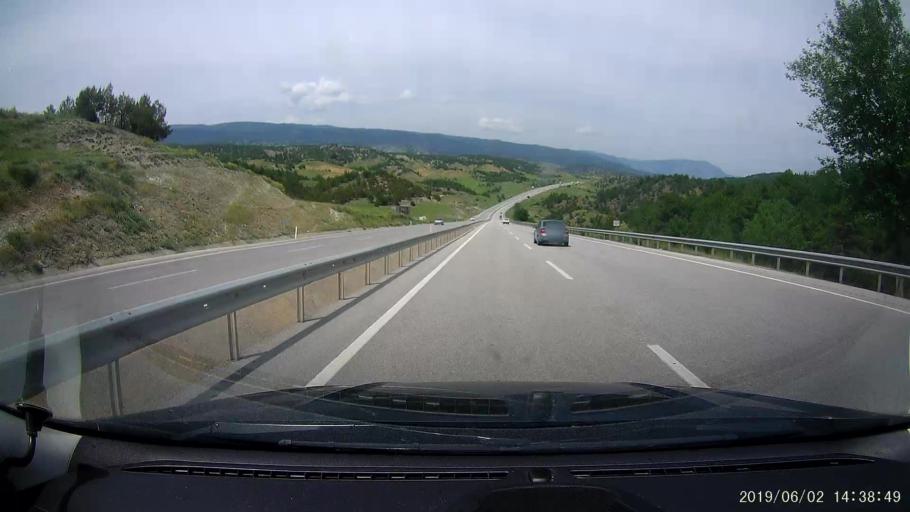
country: TR
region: Corum
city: Hacihamza
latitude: 41.0609
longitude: 34.2888
